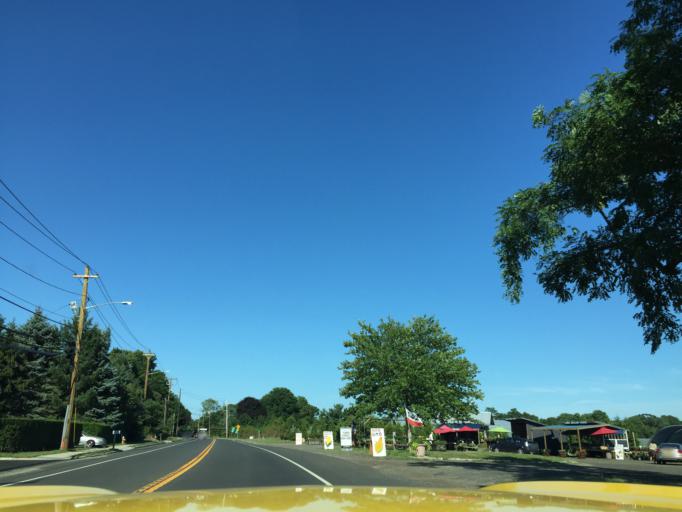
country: US
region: New York
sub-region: Suffolk County
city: Aquebogue
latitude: 40.9473
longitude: -72.6065
